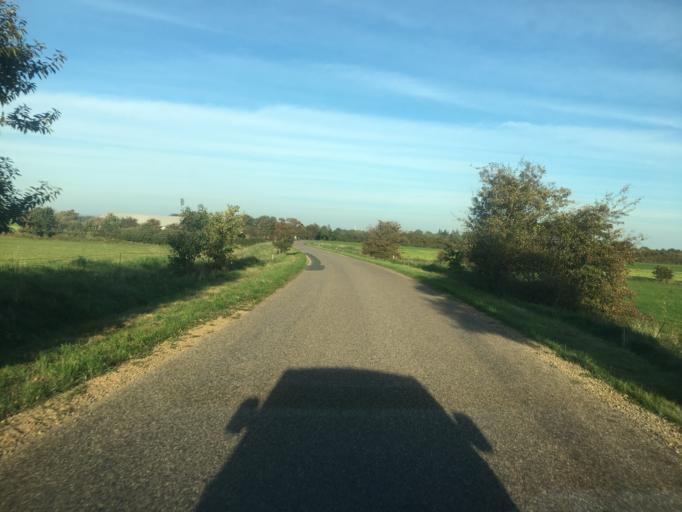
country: DE
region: Schleswig-Holstein
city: Ellhoft
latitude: 54.9135
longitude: 8.9408
